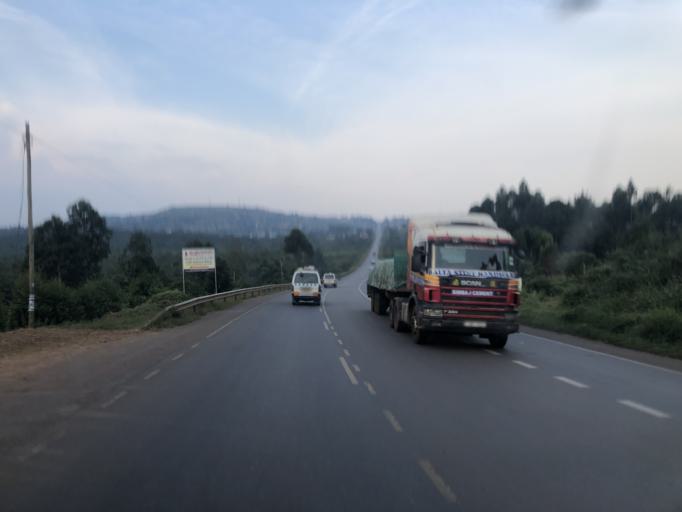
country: UG
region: Central Region
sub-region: Mpigi District
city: Mpigi
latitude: 0.2412
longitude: 32.3517
